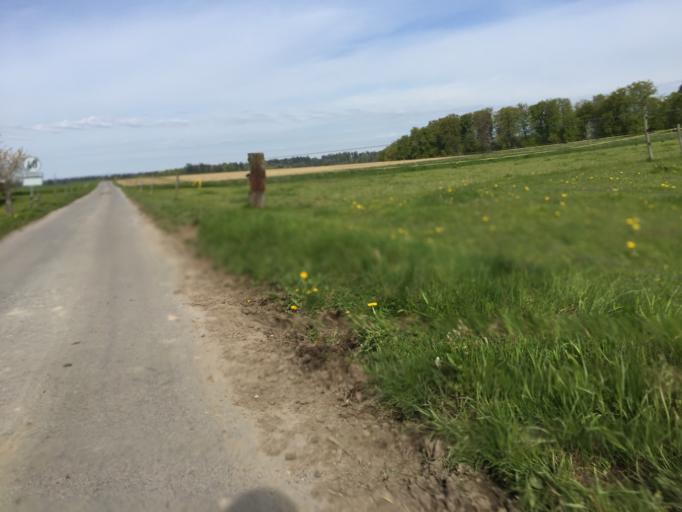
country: CH
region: Bern
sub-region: Bern-Mittelland District
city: Koniz
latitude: 46.9157
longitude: 7.3780
